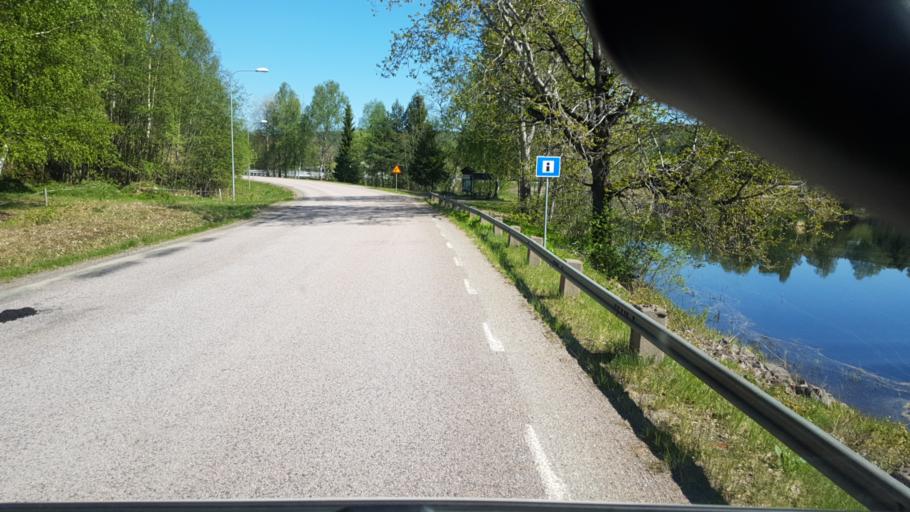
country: SE
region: Vaermland
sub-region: Eda Kommun
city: Amotfors
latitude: 59.8839
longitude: 12.5207
